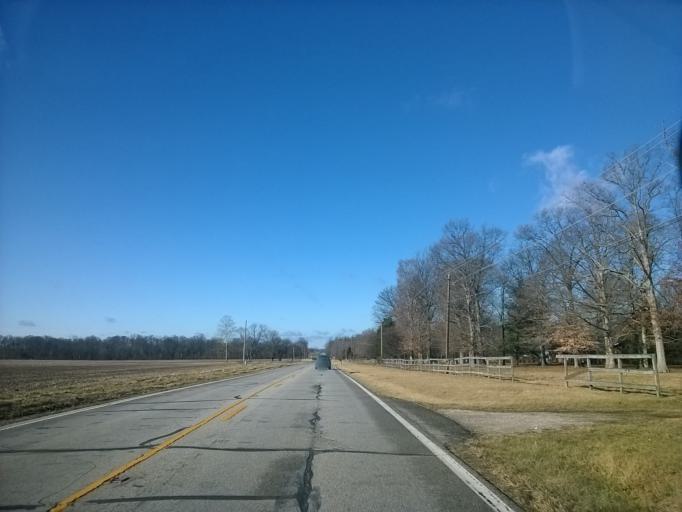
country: US
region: Indiana
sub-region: Scott County
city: Scottsburg
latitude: 38.7436
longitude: -85.7448
